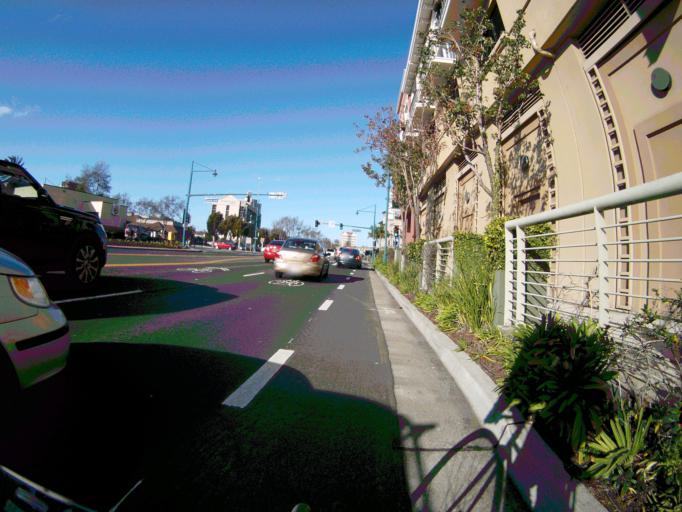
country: US
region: California
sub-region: Alameda County
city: Emeryville
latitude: 37.8367
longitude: -122.2929
